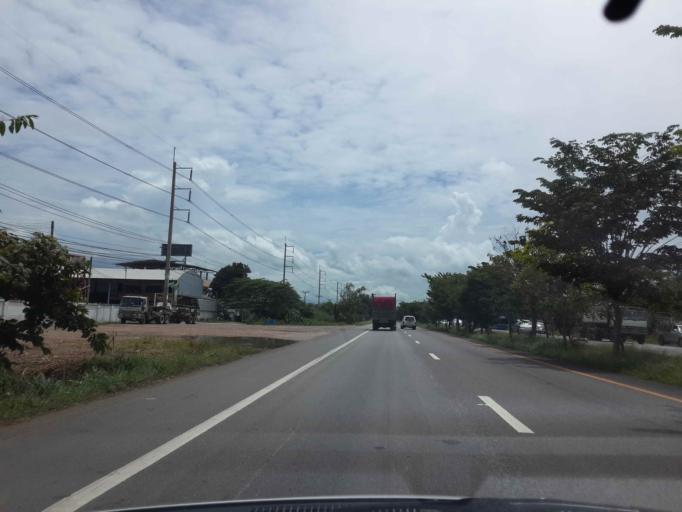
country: TH
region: Ratchaburi
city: Pak Tho
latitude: 13.4096
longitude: 99.8121
